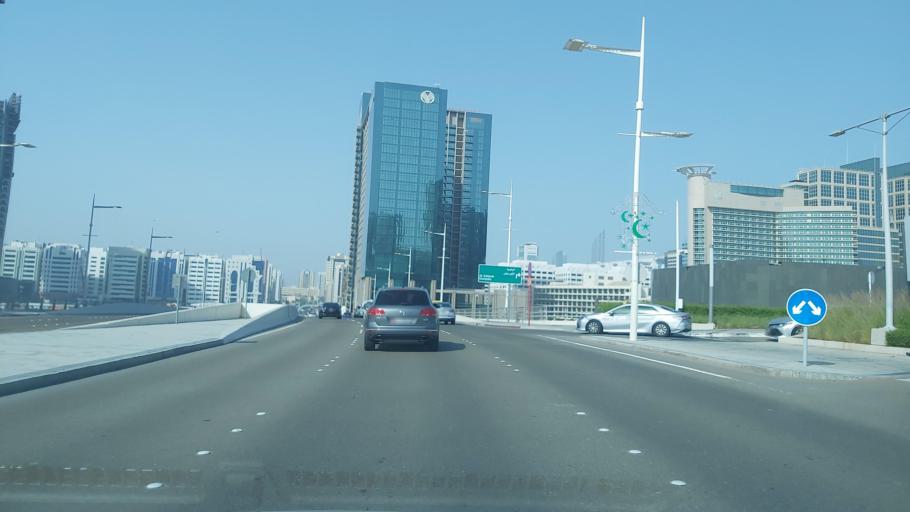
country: AE
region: Abu Dhabi
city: Abu Dhabi
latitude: 24.4954
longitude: 54.3879
